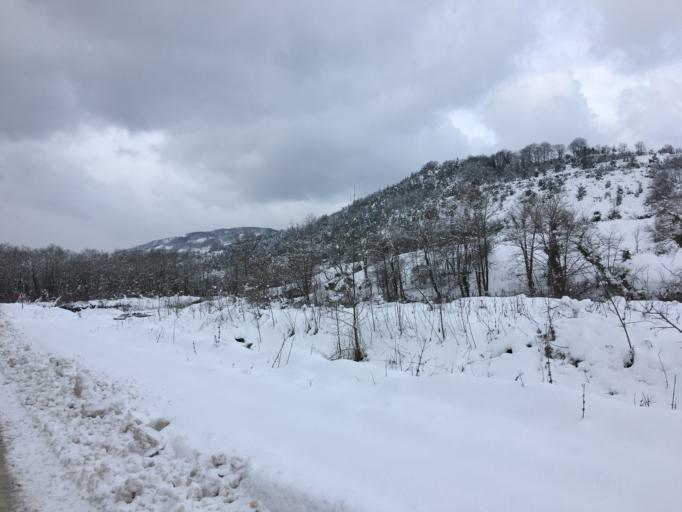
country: TR
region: Samsun
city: Alacam
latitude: 41.5969
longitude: 35.5924
